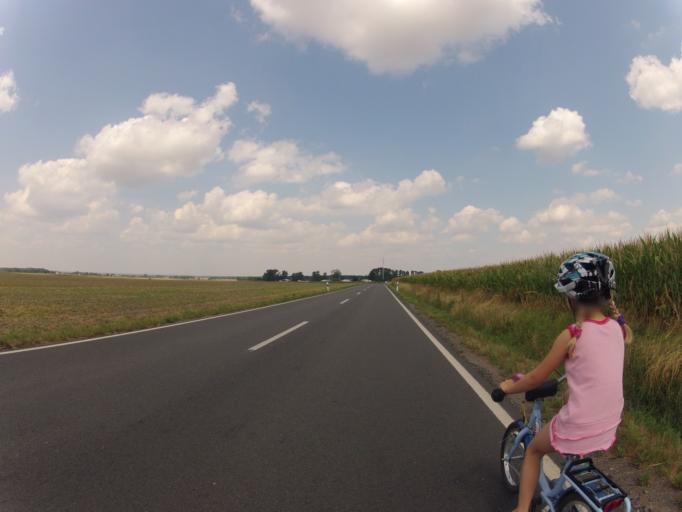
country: DE
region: Saxony
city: Schildau
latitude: 51.4625
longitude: 12.9353
